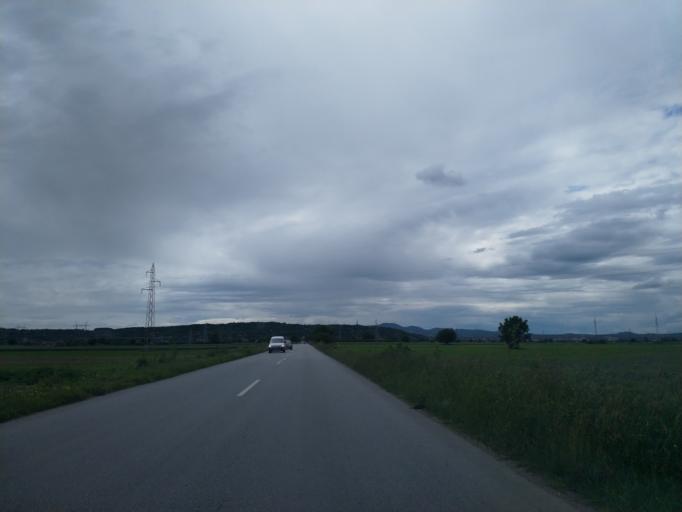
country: RS
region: Central Serbia
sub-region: Pomoravski Okrug
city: Jagodina
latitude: 43.9552
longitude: 21.3062
